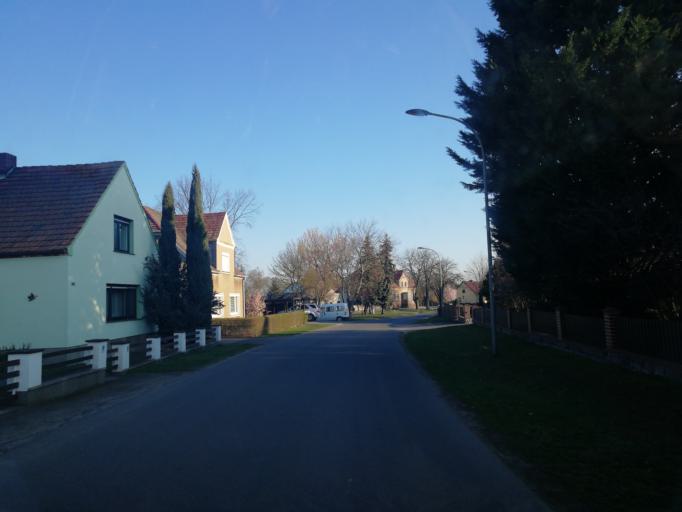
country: DE
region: Brandenburg
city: Drahnsdorf
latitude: 51.8671
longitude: 13.5908
